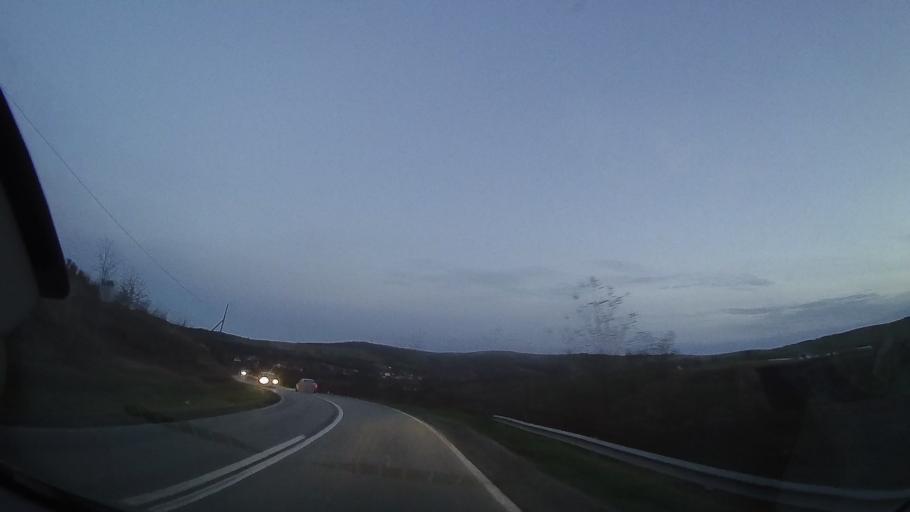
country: RO
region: Cluj
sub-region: Comuna Camarasu
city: Camarasu
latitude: 46.7919
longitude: 24.1195
